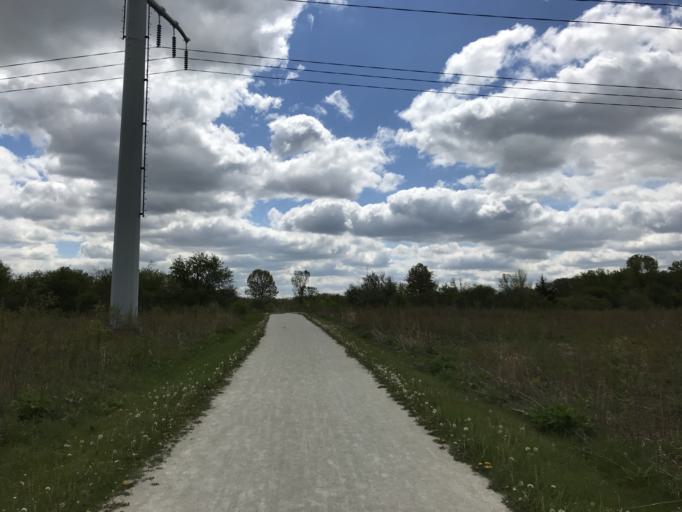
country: US
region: Illinois
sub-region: DuPage County
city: Woodridge
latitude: 41.7411
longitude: -88.0859
